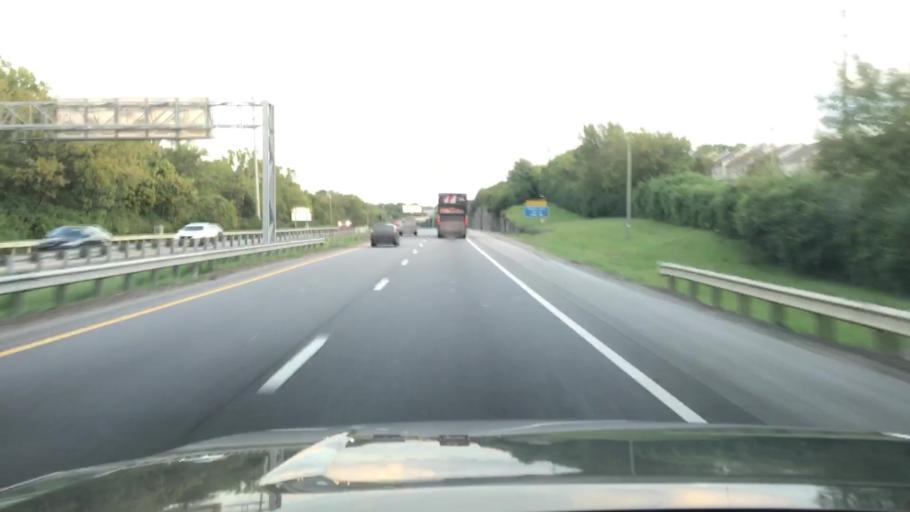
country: US
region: Tennessee
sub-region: Davidson County
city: Belle Meade
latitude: 36.1638
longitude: -86.8683
